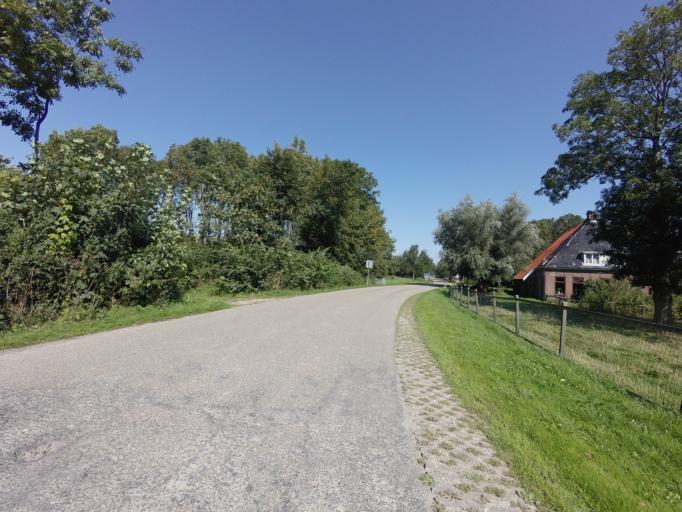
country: NL
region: Friesland
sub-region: Gemeente Dongeradeel
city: Ternaard
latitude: 53.3731
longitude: 5.9980
